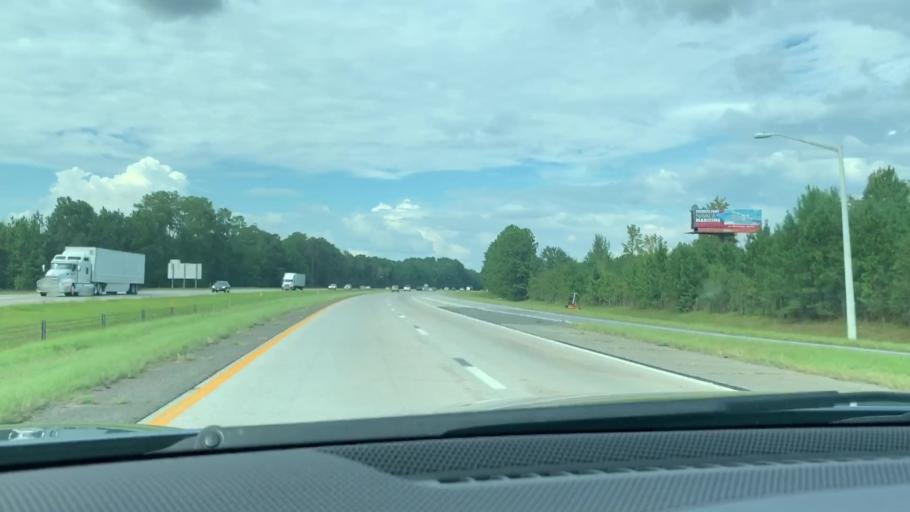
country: US
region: South Carolina
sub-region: Jasper County
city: Hardeeville
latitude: 32.3151
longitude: -81.0591
